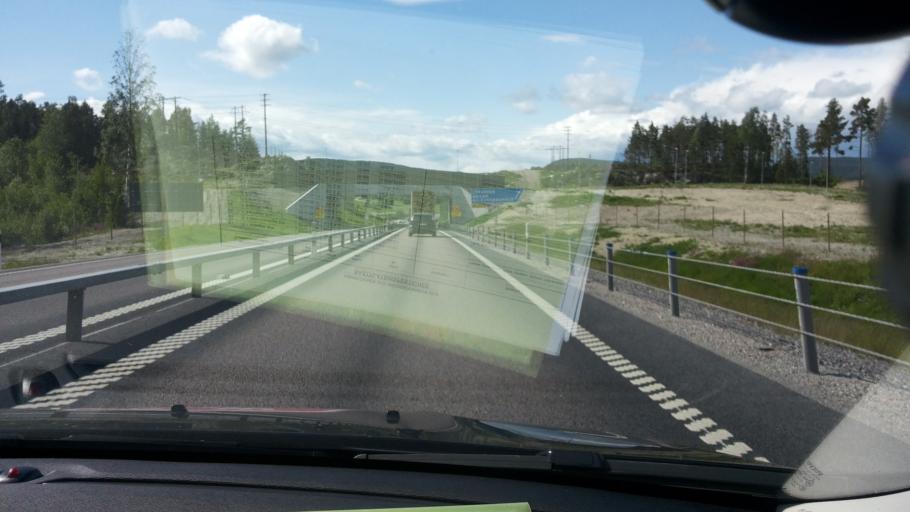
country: SE
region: Vaesternorrland
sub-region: Sundsvalls Kommun
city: Njurundabommen
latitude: 62.2620
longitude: 17.3603
